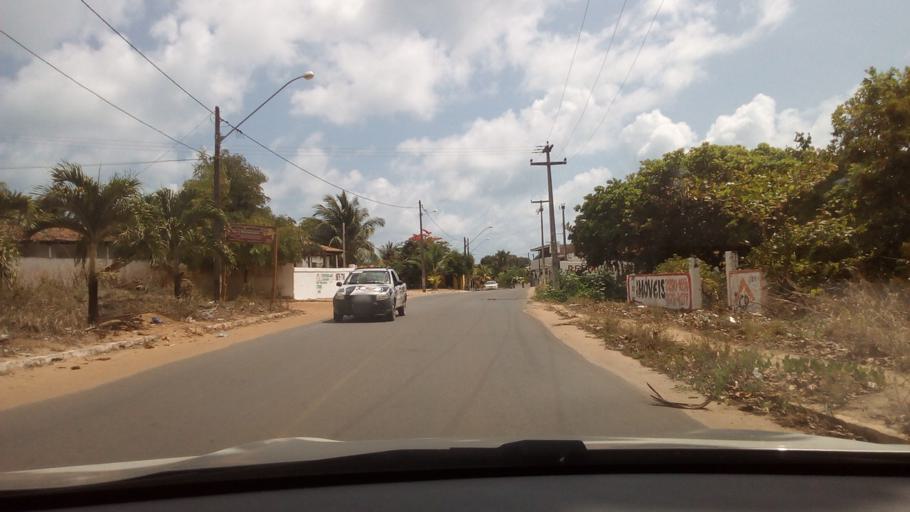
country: BR
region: Paraiba
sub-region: Conde
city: Conde
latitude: -7.2898
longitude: -34.8054
